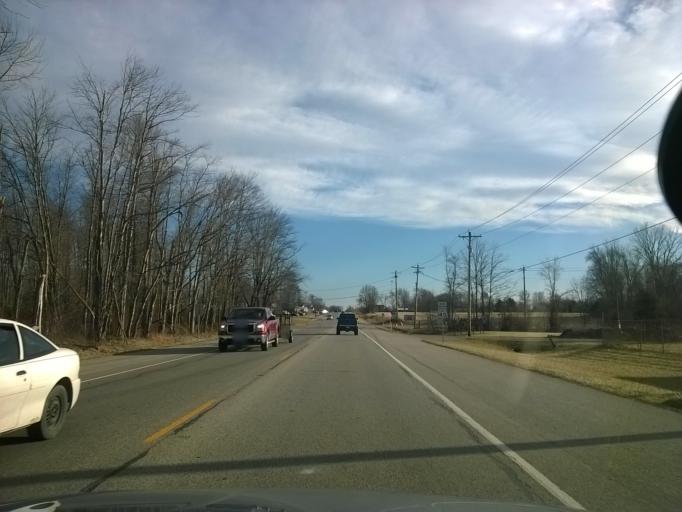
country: US
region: Indiana
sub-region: Scott County
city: Austin
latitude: 38.7586
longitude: -85.8145
